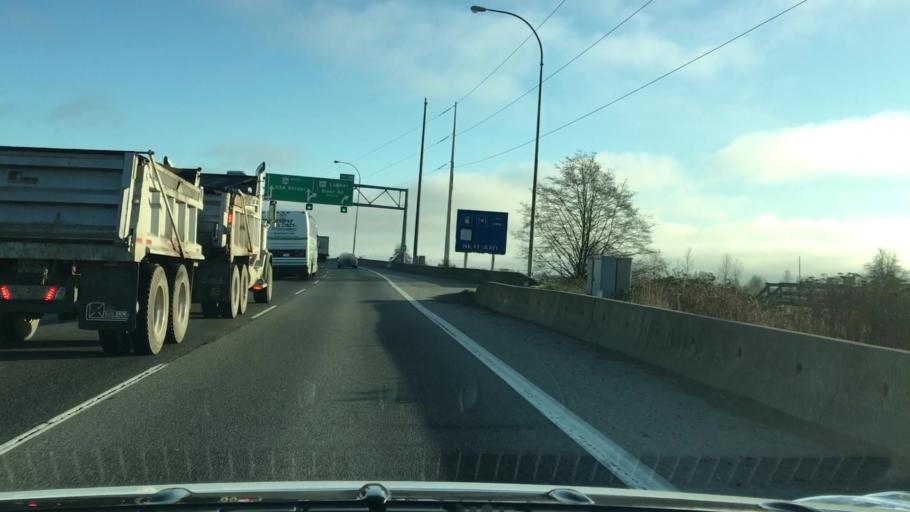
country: CA
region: British Columbia
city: Ladner
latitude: 49.1112
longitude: -123.0628
